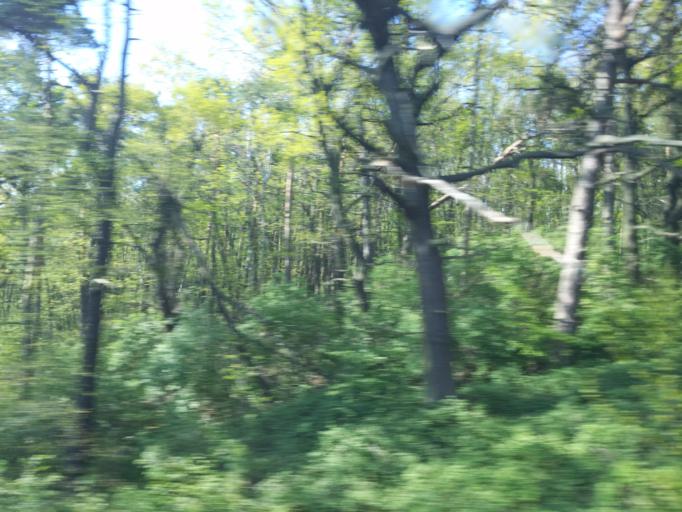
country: DE
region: Saxony
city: Goda
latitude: 51.1634
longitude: 14.3571
